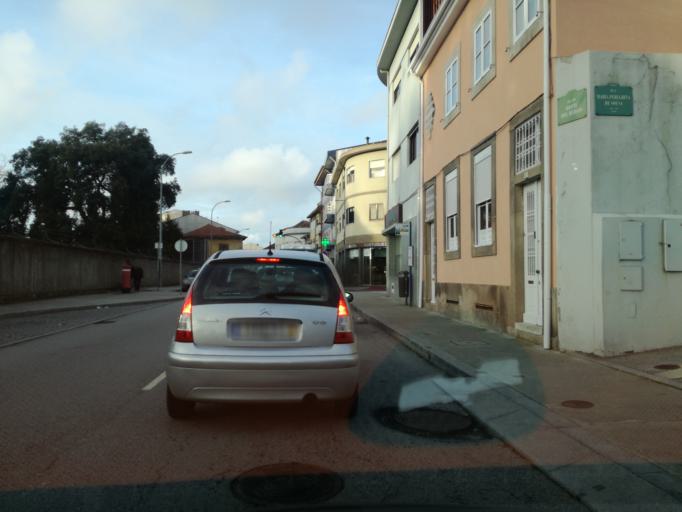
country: PT
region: Porto
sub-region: Matosinhos
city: Senhora da Hora
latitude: 41.1752
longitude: -8.6276
